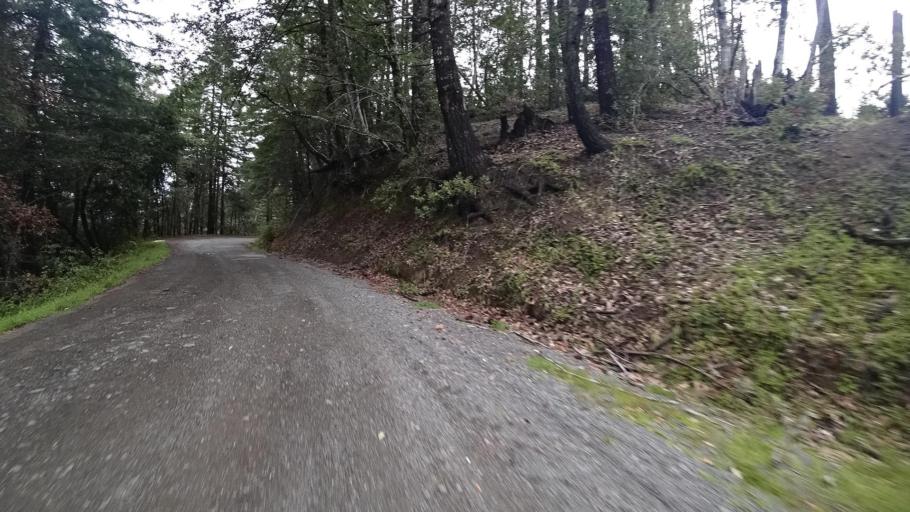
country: US
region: California
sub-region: Humboldt County
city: Blue Lake
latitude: 40.8671
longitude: -123.9049
